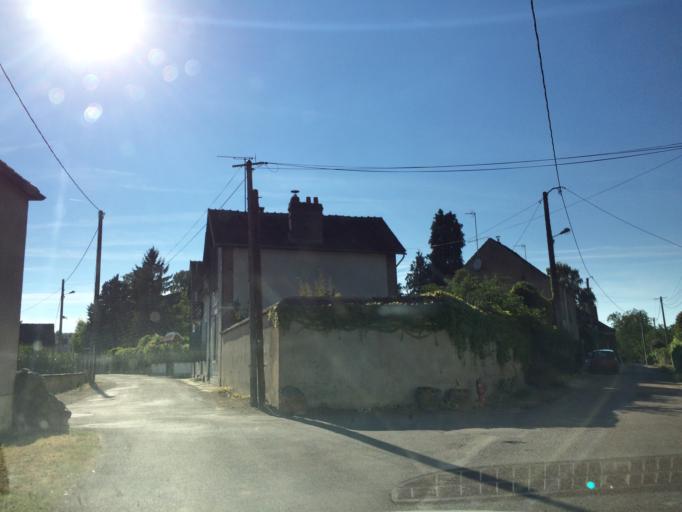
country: FR
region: Bourgogne
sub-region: Departement de l'Yonne
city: Cheny
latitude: 47.9241
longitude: 3.5198
